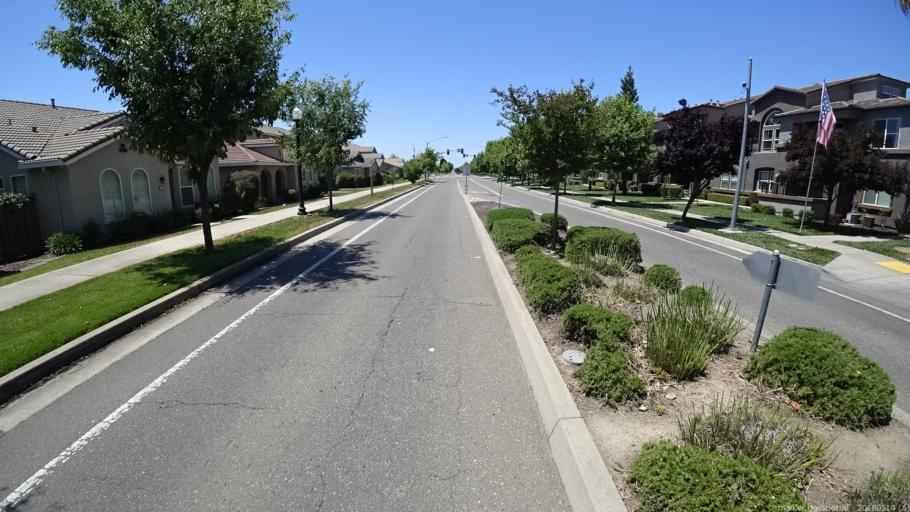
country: US
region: California
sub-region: Yolo County
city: West Sacramento
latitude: 38.6278
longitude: -121.5235
